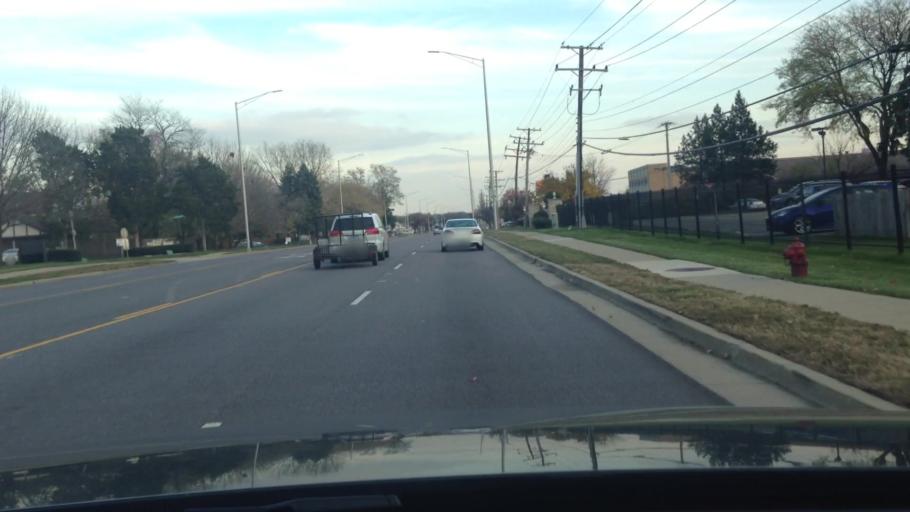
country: US
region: Illinois
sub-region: Cook County
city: Rolling Meadows
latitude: 42.0597
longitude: -88.0145
